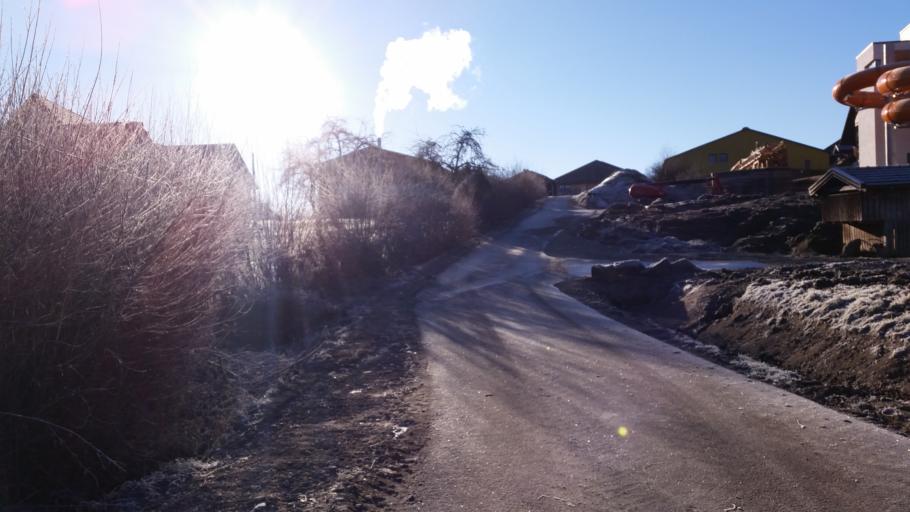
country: DE
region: Bavaria
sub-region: Lower Bavaria
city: Grafenau
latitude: 48.8395
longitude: 13.3511
